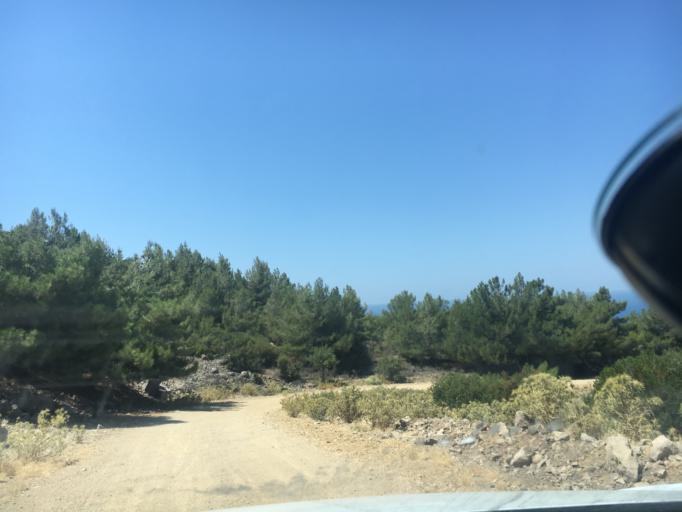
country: TR
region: Canakkale
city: Gulpinar
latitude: 39.4855
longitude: 26.0772
